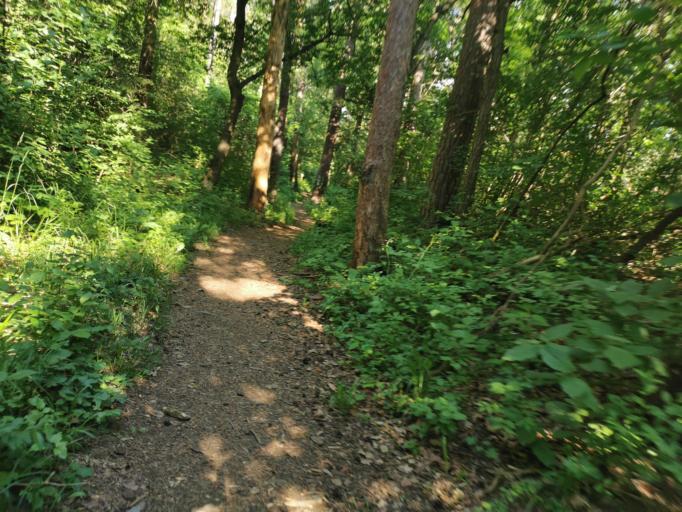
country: CZ
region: South Moravian
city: Knezdub
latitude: 48.8540
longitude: 17.3539
